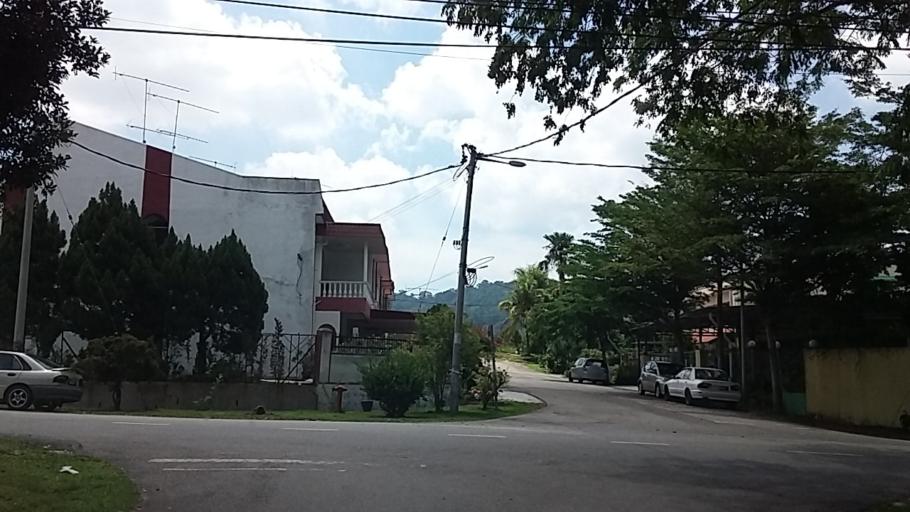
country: MY
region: Johor
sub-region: Daerah Batu Pahat
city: Batu Pahat
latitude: 1.8441
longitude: 102.9488
